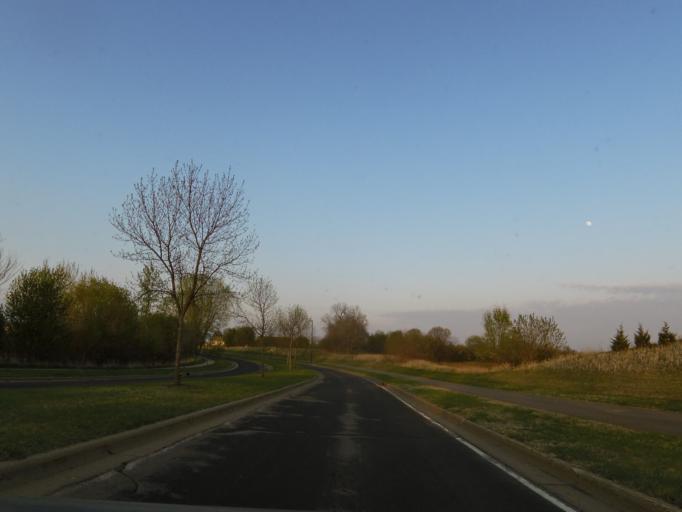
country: US
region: Minnesota
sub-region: Scott County
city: Prior Lake
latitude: 44.7395
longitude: -93.4275
